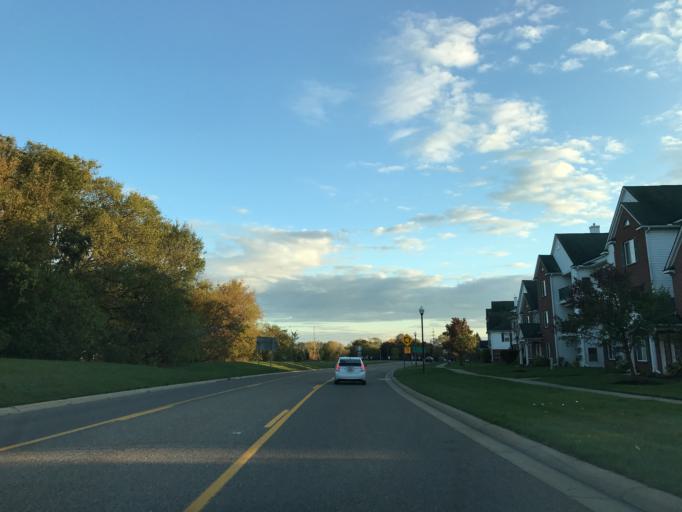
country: US
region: Michigan
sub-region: Oakland County
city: South Lyon
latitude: 42.5119
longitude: -83.6217
